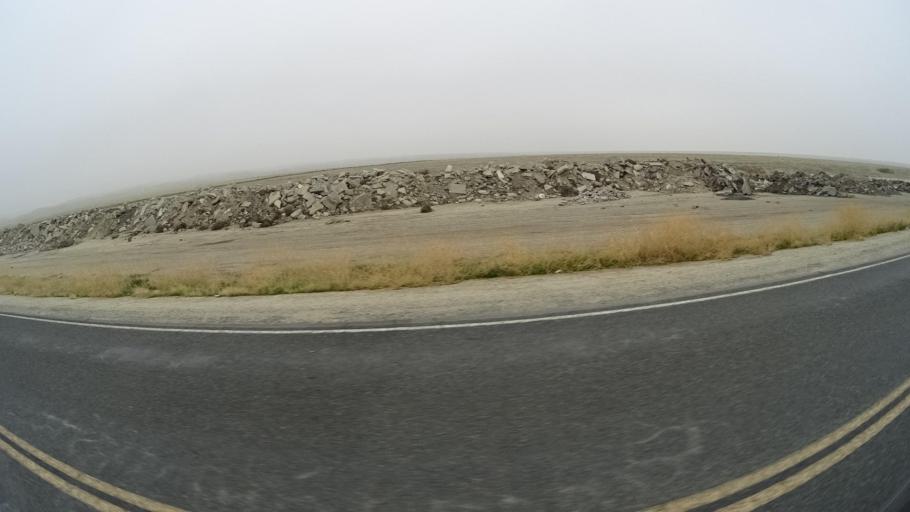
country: US
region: California
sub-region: Kern County
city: Buttonwillow
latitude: 35.3412
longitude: -119.4665
